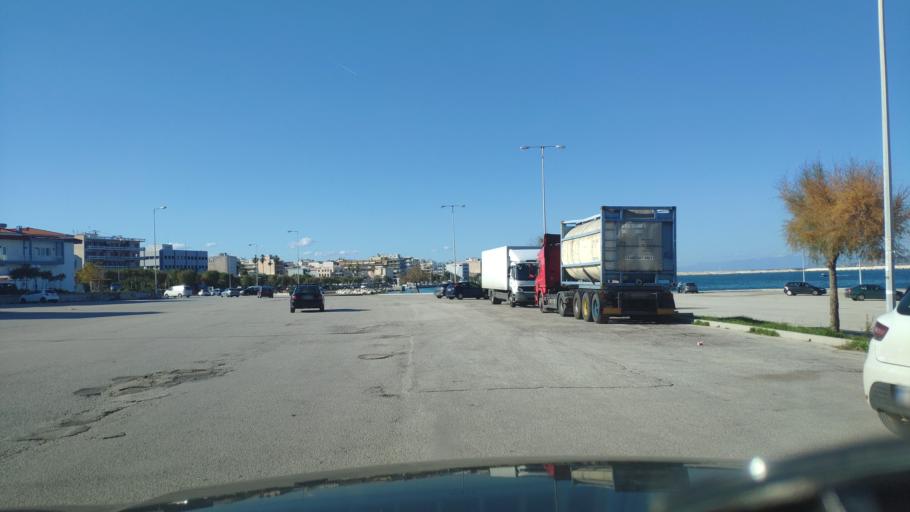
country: GR
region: Peloponnese
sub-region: Nomos Korinthias
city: Korinthos
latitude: 37.9399
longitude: 22.9395
